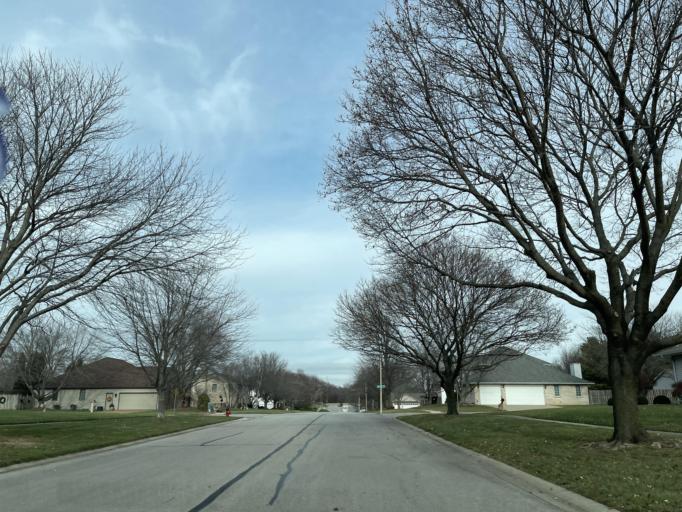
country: US
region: Illinois
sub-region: Sangamon County
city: Leland Grove
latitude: 39.7835
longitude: -89.7288
